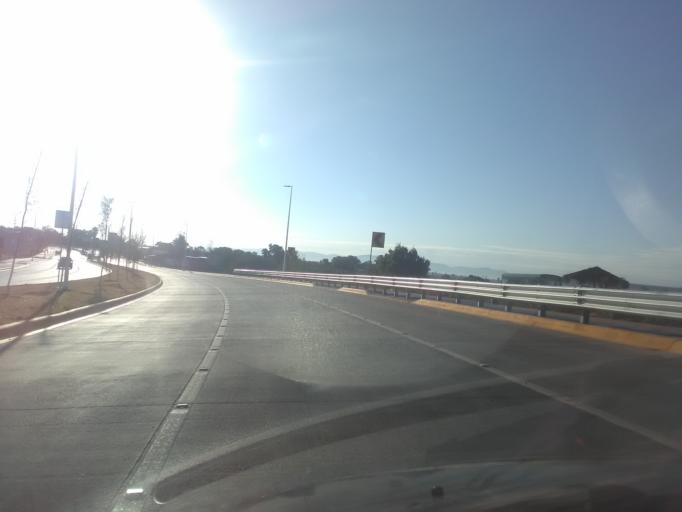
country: MX
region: Durango
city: Victoria de Durango
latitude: 23.9922
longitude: -104.7092
